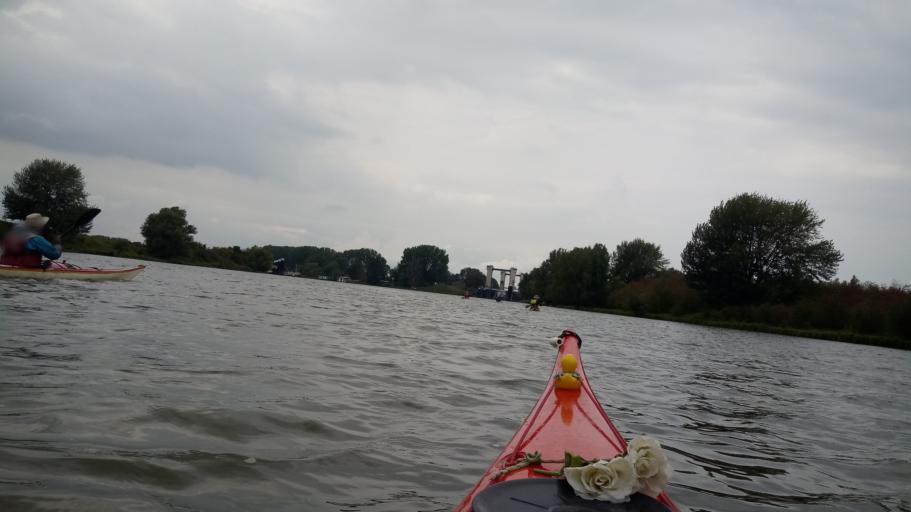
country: NL
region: Gelderland
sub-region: Gemeente Maasdriel
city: Heerewaarden
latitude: 51.7938
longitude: 5.3651
